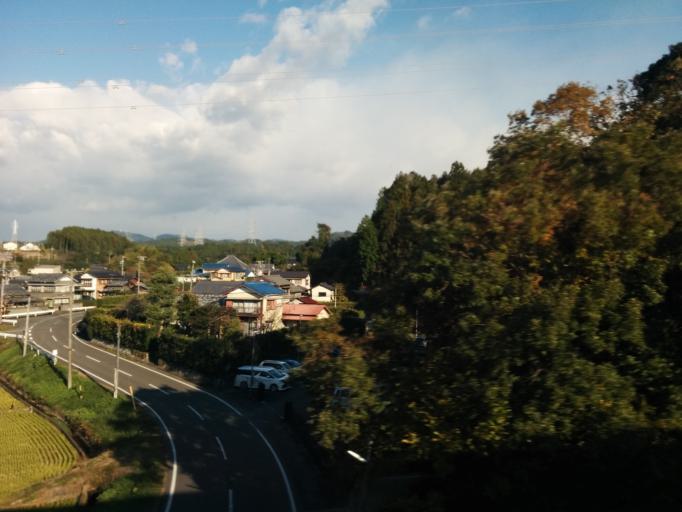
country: JP
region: Shizuoka
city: Kanaya
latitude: 34.7763
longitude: 138.1110
